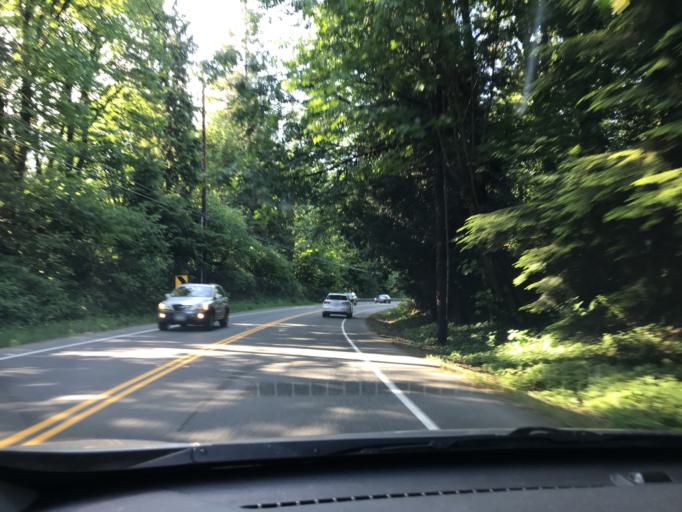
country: US
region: Washington
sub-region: King County
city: Mirrormont
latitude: 47.4781
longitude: -122.0288
